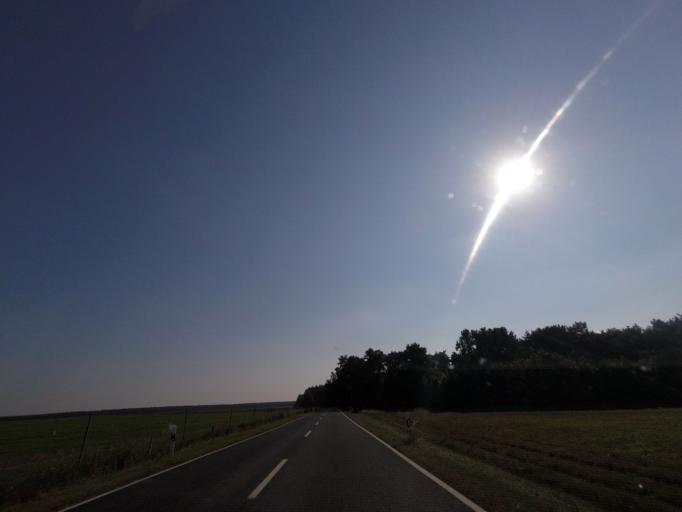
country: DE
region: Brandenburg
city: Niedergorsdorf
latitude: 51.8956
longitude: 13.0241
